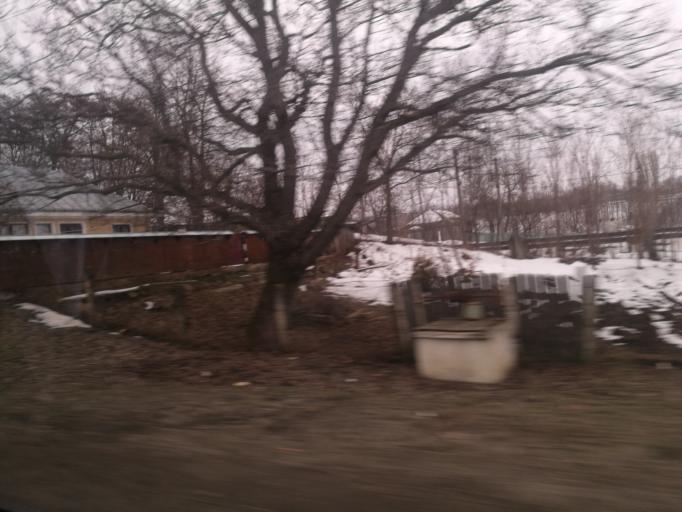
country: RO
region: Iasi
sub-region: Comuna Ruginoasa
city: Ruginoasa
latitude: 47.2440
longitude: 26.8512
